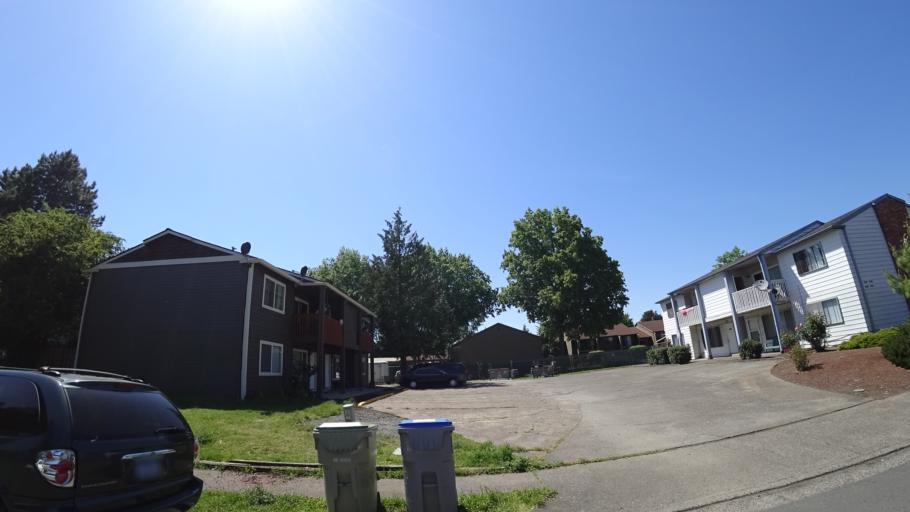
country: US
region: Oregon
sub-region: Washington County
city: Beaverton
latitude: 45.4961
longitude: -122.8067
